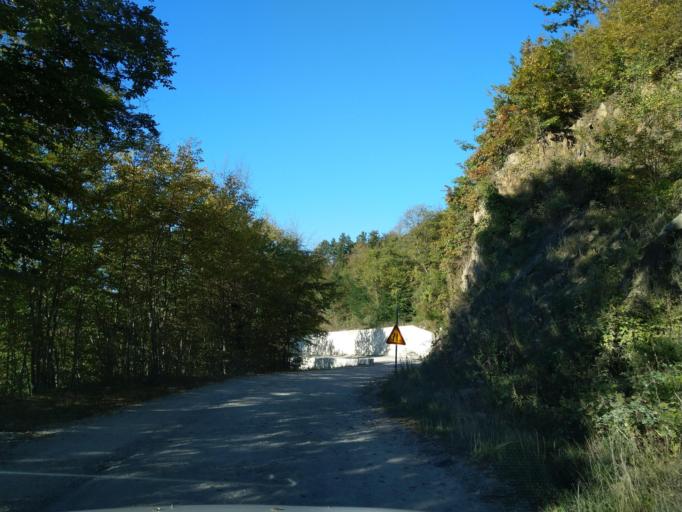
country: RS
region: Central Serbia
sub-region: Moravicki Okrug
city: Ivanjica
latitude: 43.4748
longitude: 20.2384
